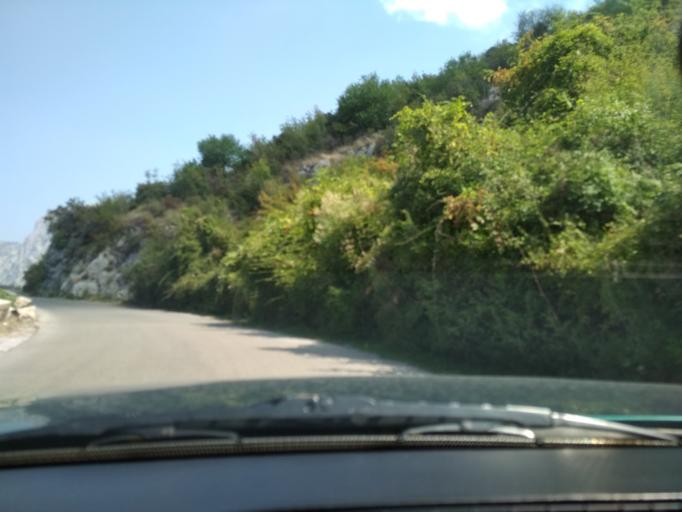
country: ME
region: Kotor
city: Kotor
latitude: 42.4009
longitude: 18.7736
